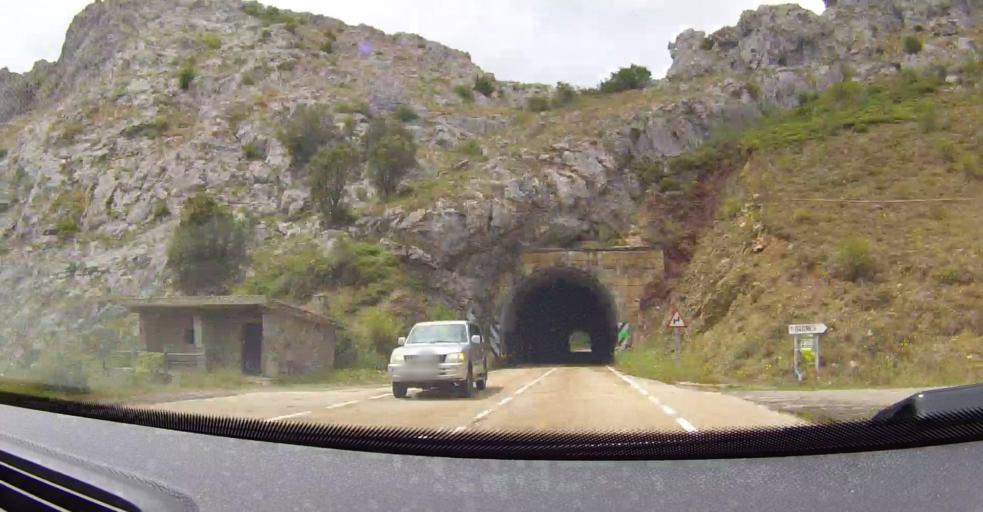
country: ES
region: Castille and Leon
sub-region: Provincia de Leon
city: Puebla de Lillo
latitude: 42.9605
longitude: -5.2512
